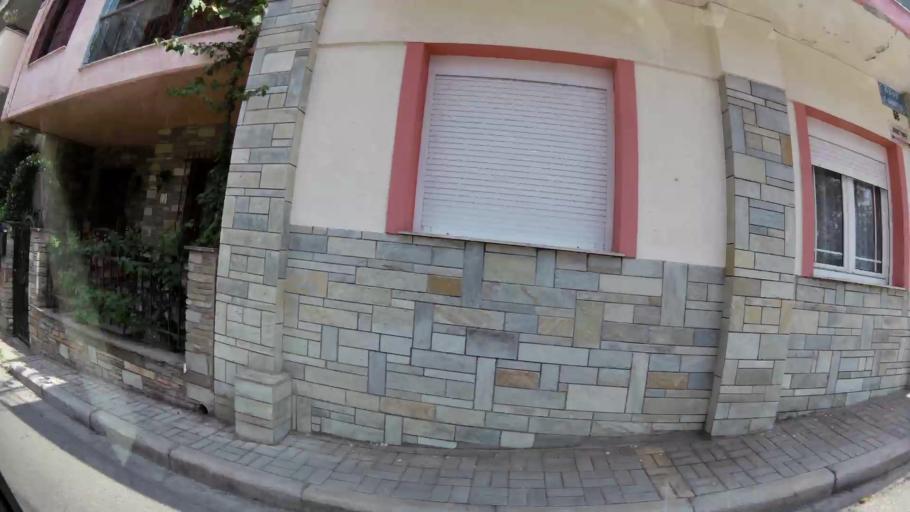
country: GR
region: Central Macedonia
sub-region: Nomos Thessalonikis
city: Agios Pavlos
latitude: 40.6431
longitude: 22.9549
